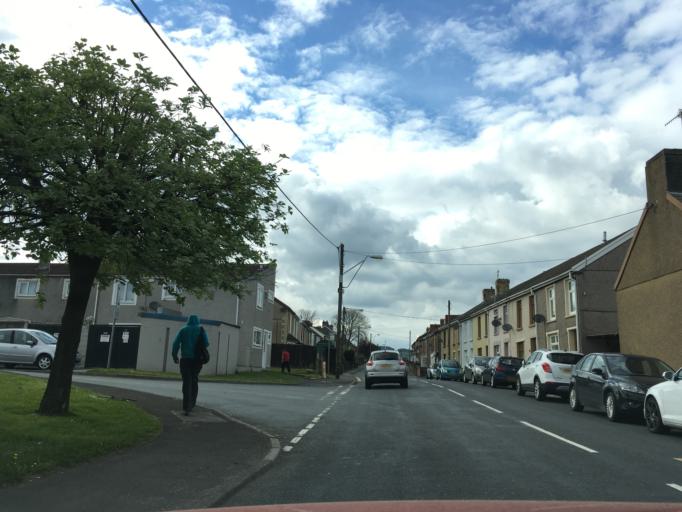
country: GB
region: Wales
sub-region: Caerphilly County Borough
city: Nelson
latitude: 51.6529
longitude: -3.2844
